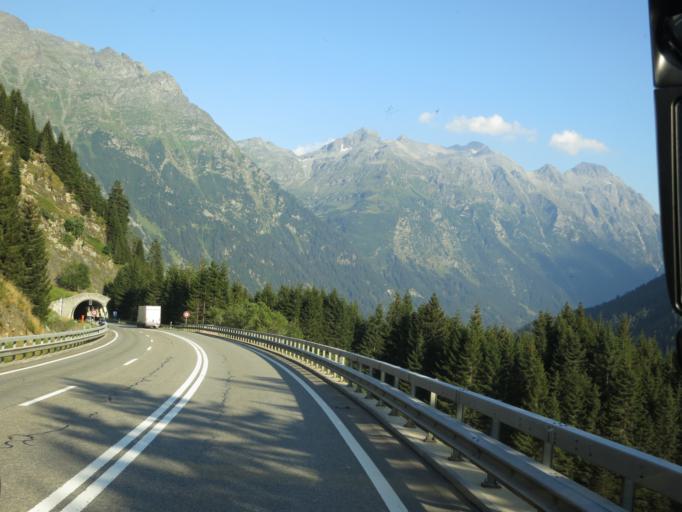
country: CH
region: Grisons
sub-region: Moesa District
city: Mesocco
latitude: 46.4338
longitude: 9.1979
